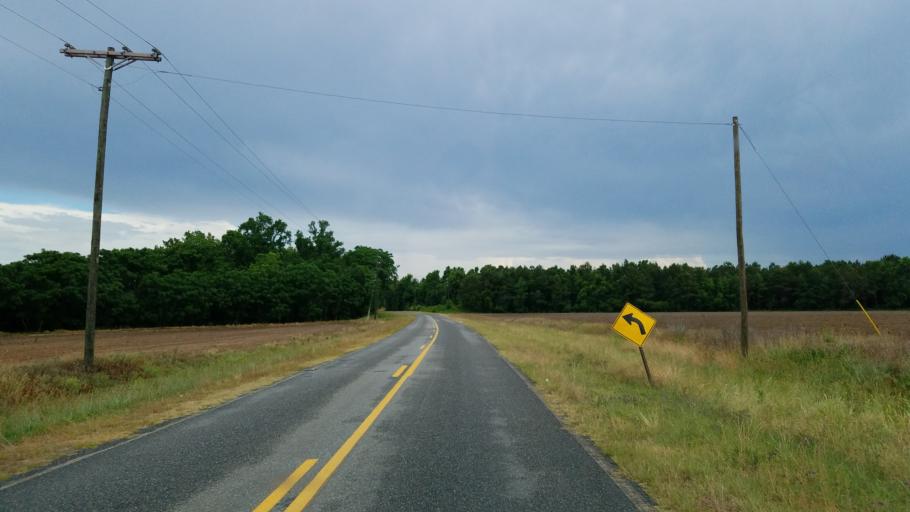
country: US
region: Georgia
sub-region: Dooly County
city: Vienna
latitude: 32.1738
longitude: -83.7987
